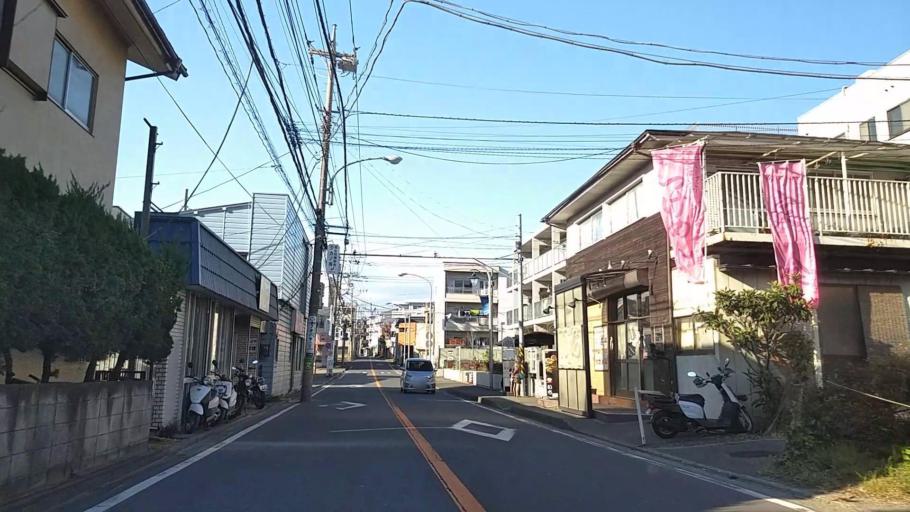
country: JP
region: Tokyo
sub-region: Machida-shi
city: Machida
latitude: 35.5242
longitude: 139.5518
